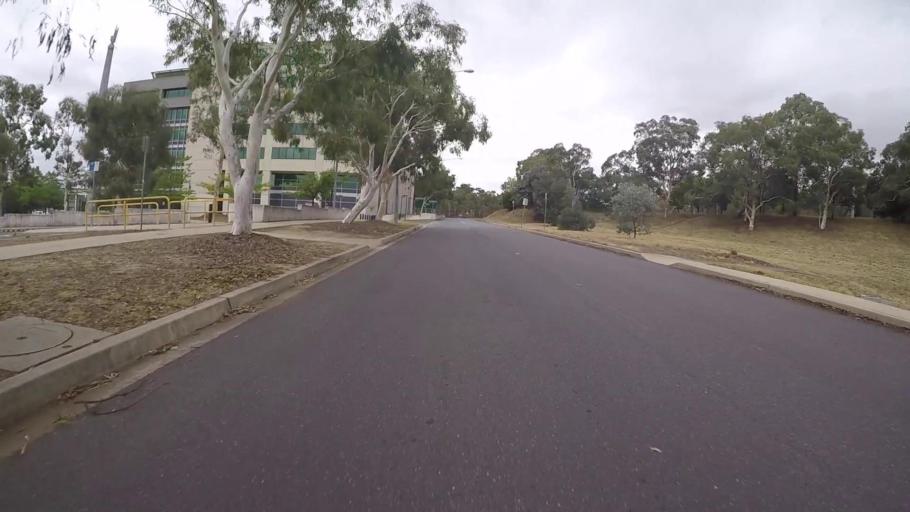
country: AU
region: Australian Capital Territory
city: Canberra
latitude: -35.2986
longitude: 149.1528
